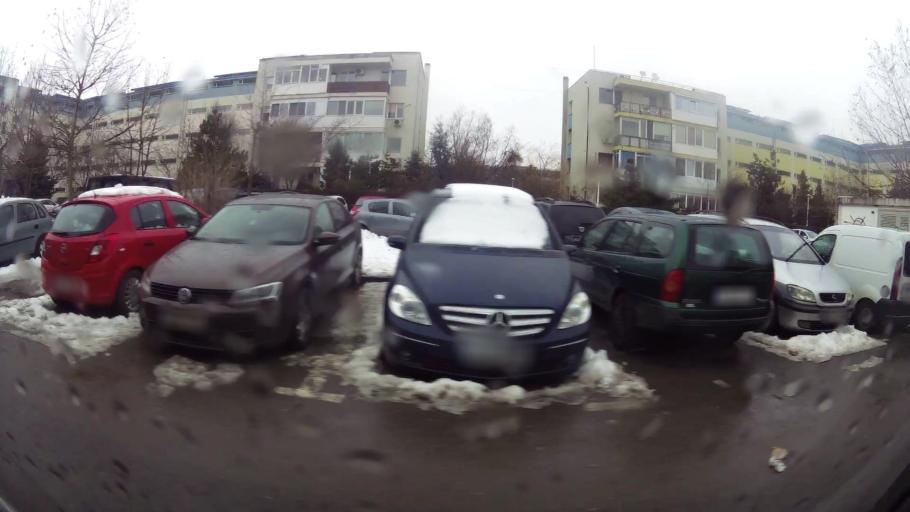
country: RO
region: Ilfov
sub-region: Comuna Chiajna
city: Rosu
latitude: 44.4201
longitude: 26.0119
